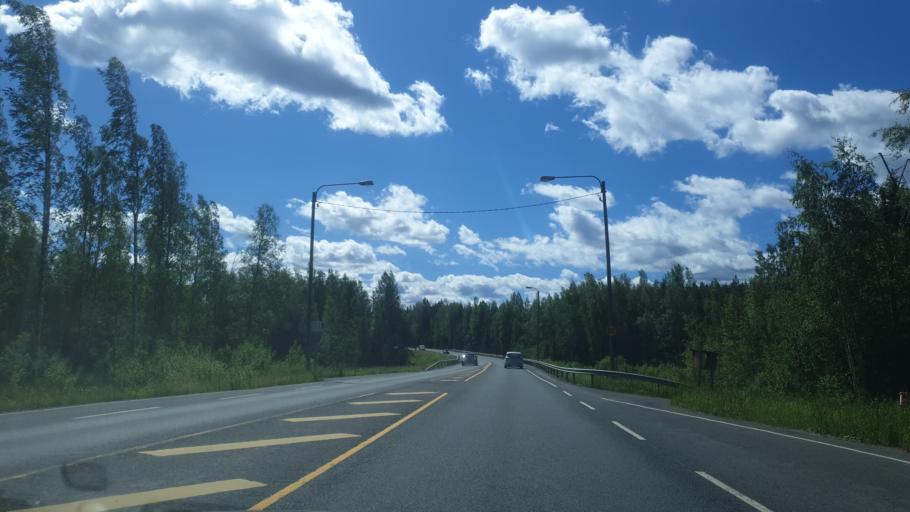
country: FI
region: Northern Savo
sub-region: Varkaus
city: Leppaevirta
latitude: 62.5818
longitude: 27.6043
